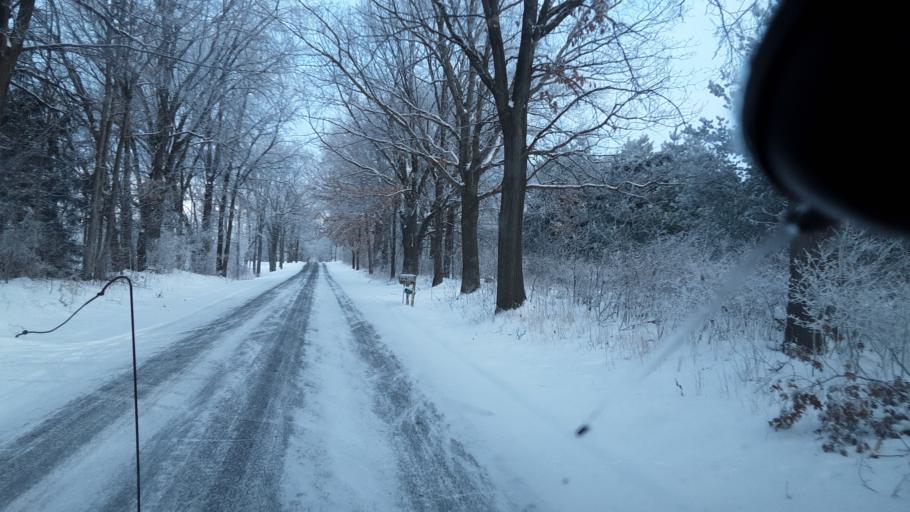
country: US
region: Michigan
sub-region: Ingham County
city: Leslie
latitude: 42.4261
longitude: -84.4970
